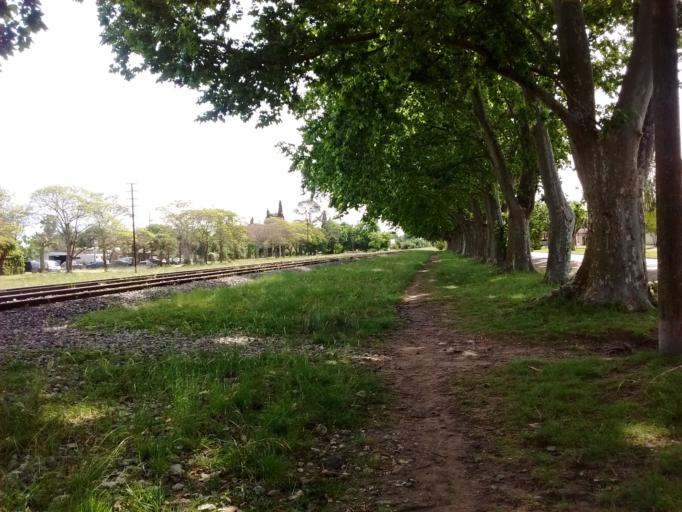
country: AR
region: Santa Fe
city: Funes
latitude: -32.9185
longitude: -60.8017
